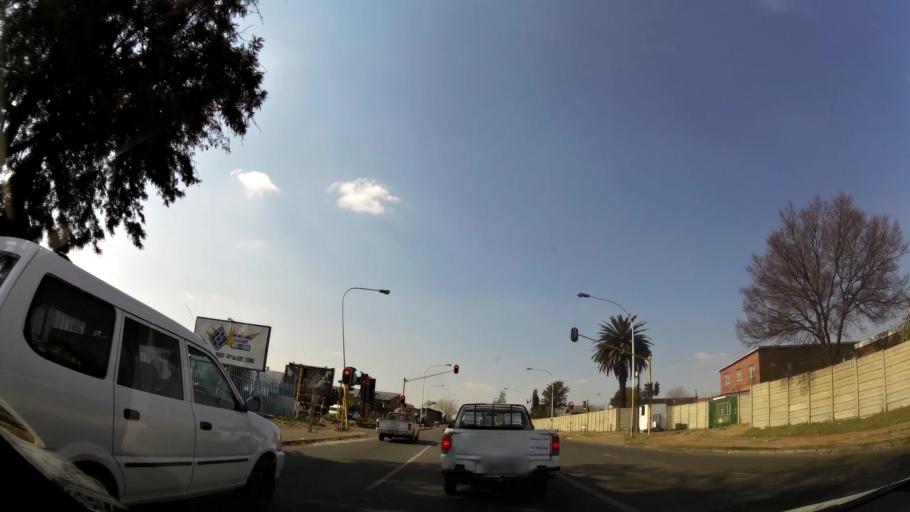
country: ZA
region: Gauteng
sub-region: Ekurhuleni Metropolitan Municipality
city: Boksburg
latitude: -26.2087
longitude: 28.2747
